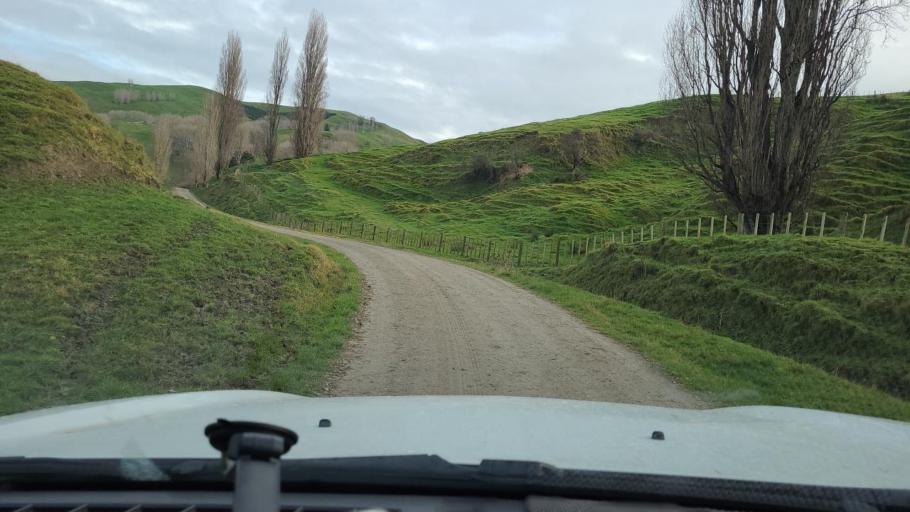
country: NZ
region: Gisborne
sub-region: Gisborne District
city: Gisborne
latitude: -38.5109
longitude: 177.7315
